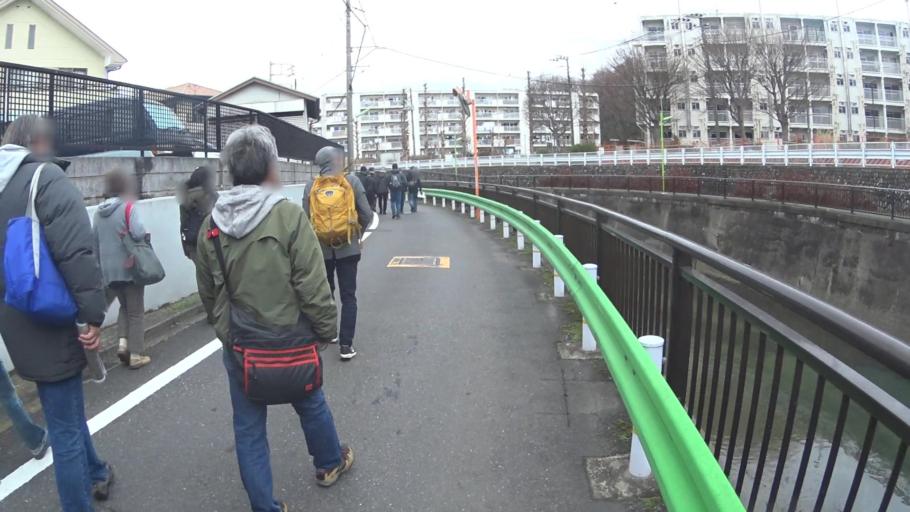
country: JP
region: Tokyo
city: Chofugaoka
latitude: 35.6319
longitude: 139.6086
